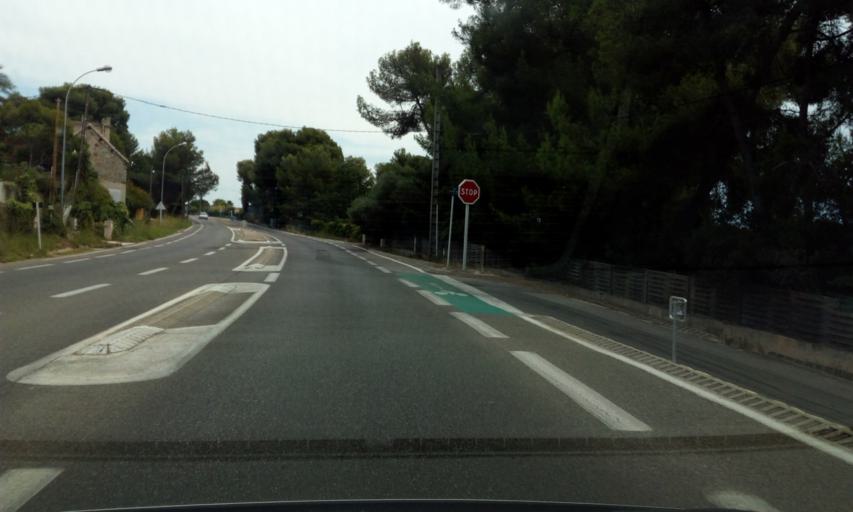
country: FR
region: Provence-Alpes-Cote d'Azur
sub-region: Departement du Var
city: Carqueiranne
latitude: 43.0855
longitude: 6.0974
